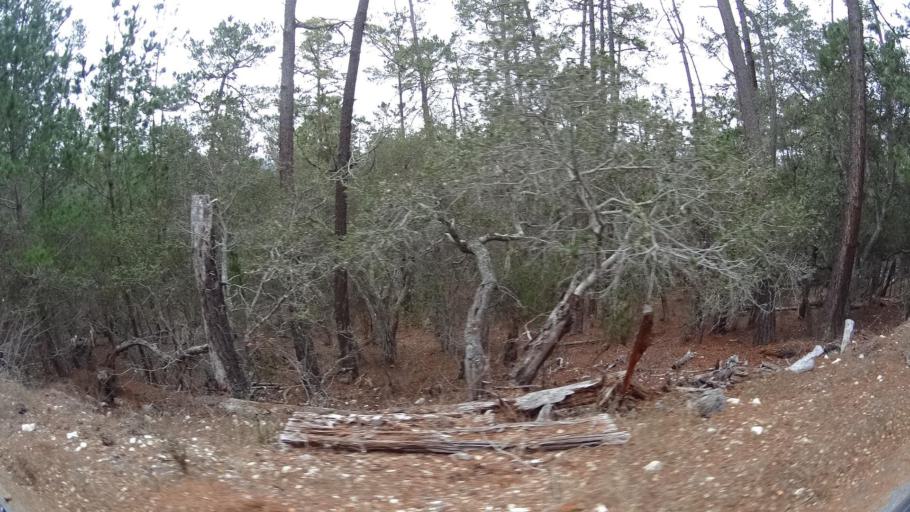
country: US
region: California
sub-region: Monterey County
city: Del Rey Oaks
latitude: 36.5644
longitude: -121.8655
